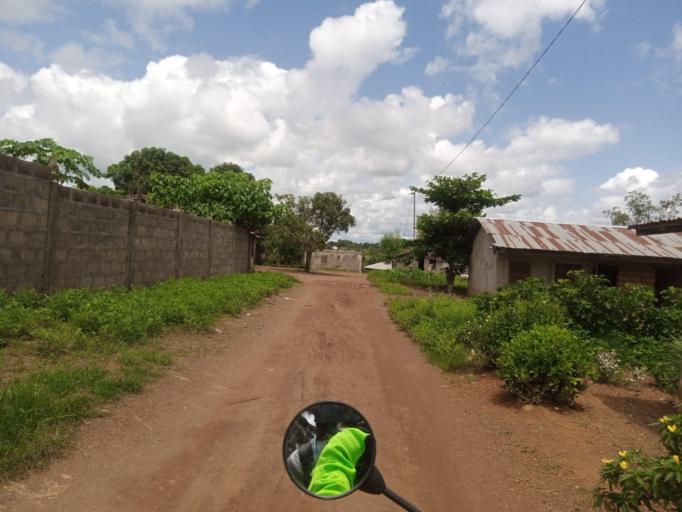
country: SL
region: Northern Province
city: Port Loko
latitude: 8.7586
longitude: -12.7834
